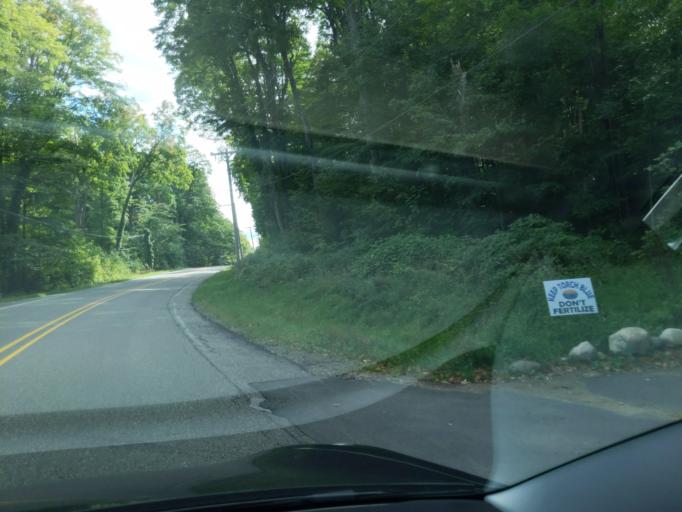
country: US
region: Michigan
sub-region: Antrim County
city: Bellaire
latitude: 44.9303
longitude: -85.2859
